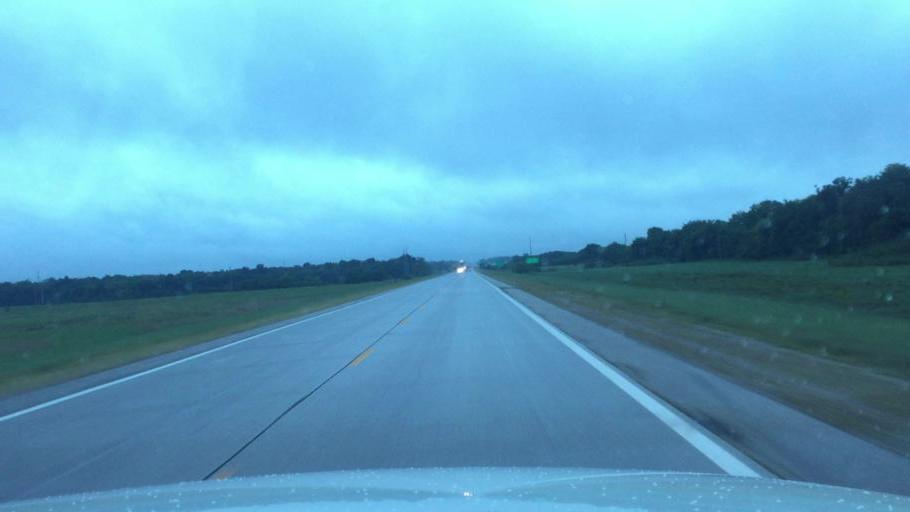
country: US
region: Kansas
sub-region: Neosho County
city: Chanute
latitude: 37.7102
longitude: -95.4794
